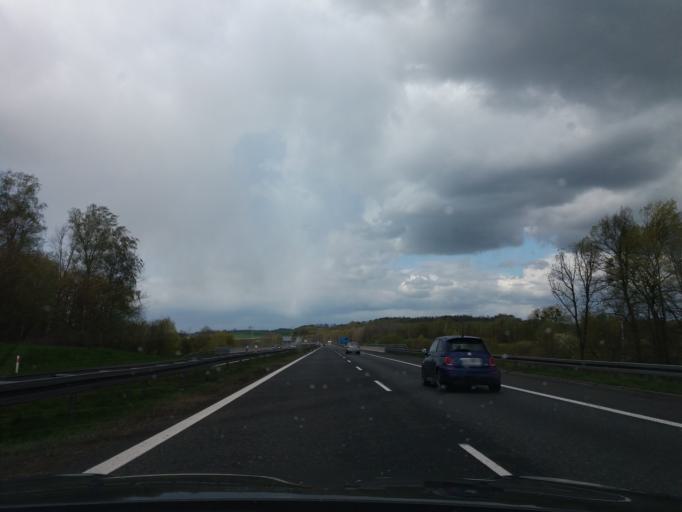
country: PL
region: Silesian Voivodeship
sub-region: Powiat gliwicki
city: Rudziniec
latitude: 50.3847
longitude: 18.4601
